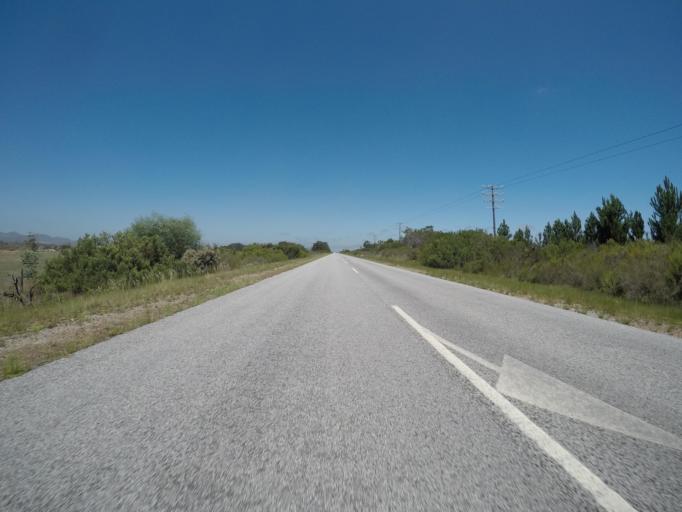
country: ZA
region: Eastern Cape
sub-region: Cacadu District Municipality
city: Kruisfontein
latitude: -34.0083
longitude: 24.5575
